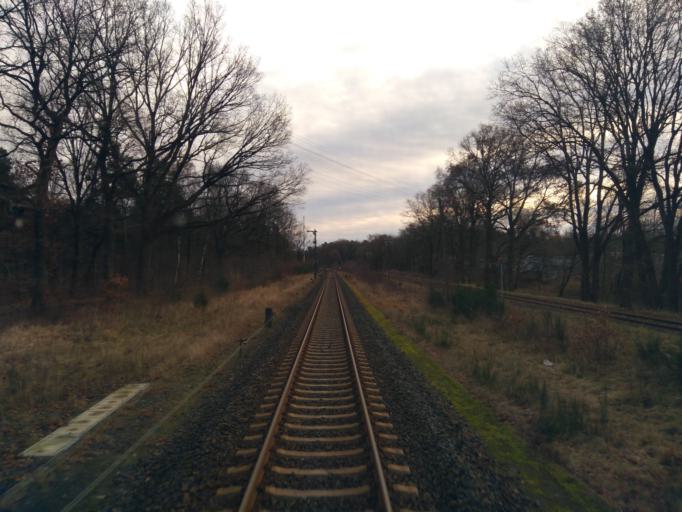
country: DE
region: Lower Saxony
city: Munster
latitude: 52.9911
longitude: 10.1080
